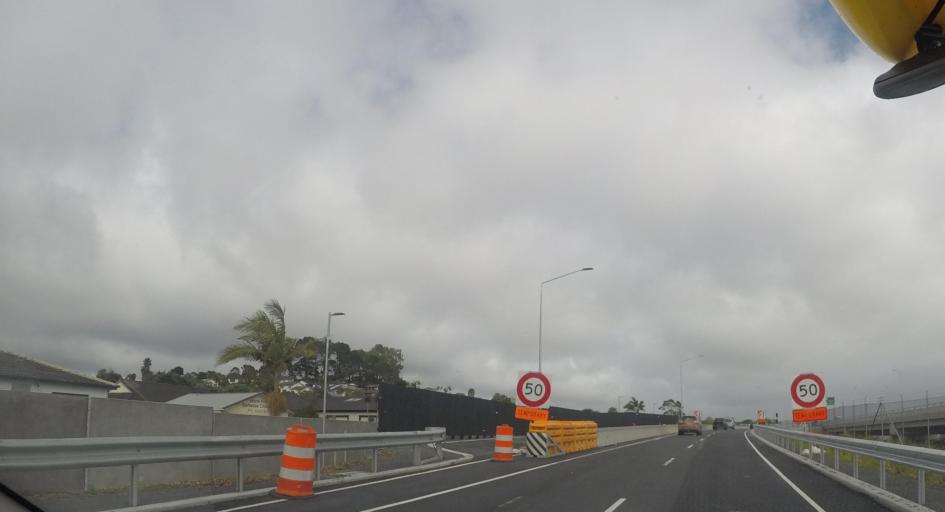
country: NZ
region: Auckland
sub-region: Auckland
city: Rothesay Bay
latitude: -36.7522
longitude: 174.7208
